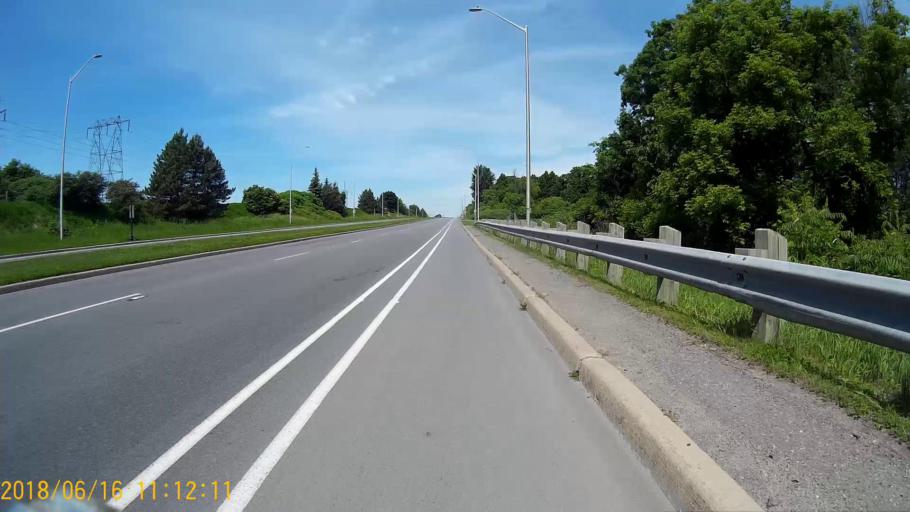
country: CA
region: Ontario
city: Bells Corners
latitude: 45.3331
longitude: -75.8971
